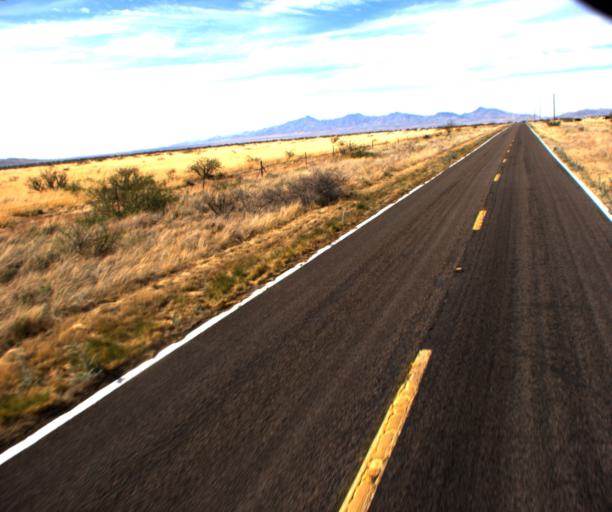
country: US
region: Arizona
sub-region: Cochise County
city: Willcox
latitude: 31.9274
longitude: -109.4914
